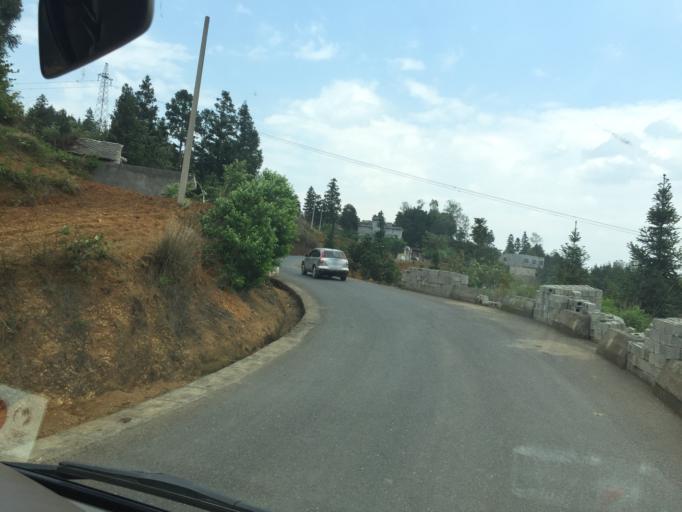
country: CN
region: Guangxi Zhuangzu Zizhiqu
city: Xinzhou
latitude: 25.6594
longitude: 105.2382
